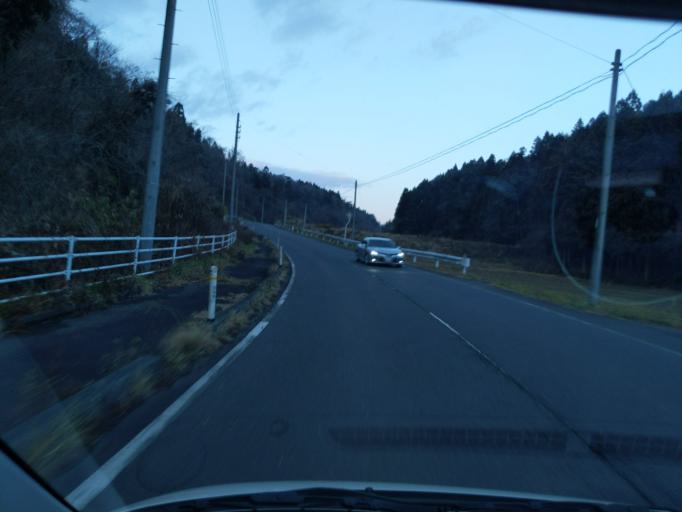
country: JP
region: Iwate
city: Ichinoseki
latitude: 38.8169
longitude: 141.1165
